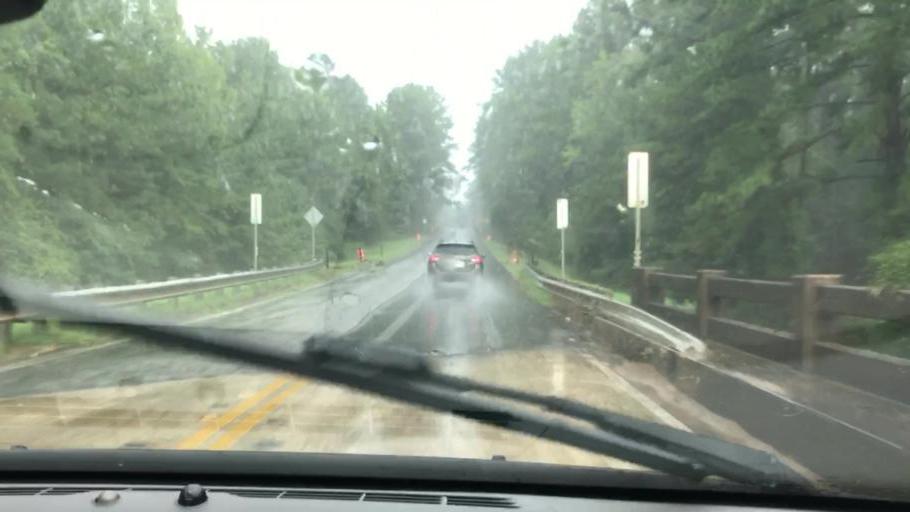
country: US
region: Georgia
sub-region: Clay County
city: Fort Gaines
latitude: 31.5500
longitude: -85.0187
